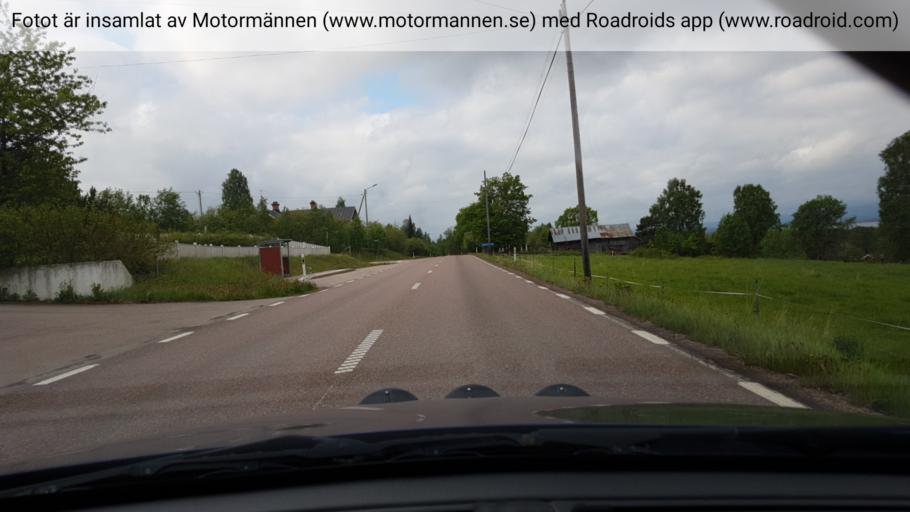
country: SE
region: Dalarna
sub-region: Orsa Kommun
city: Orsa
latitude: 61.0839
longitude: 14.6231
